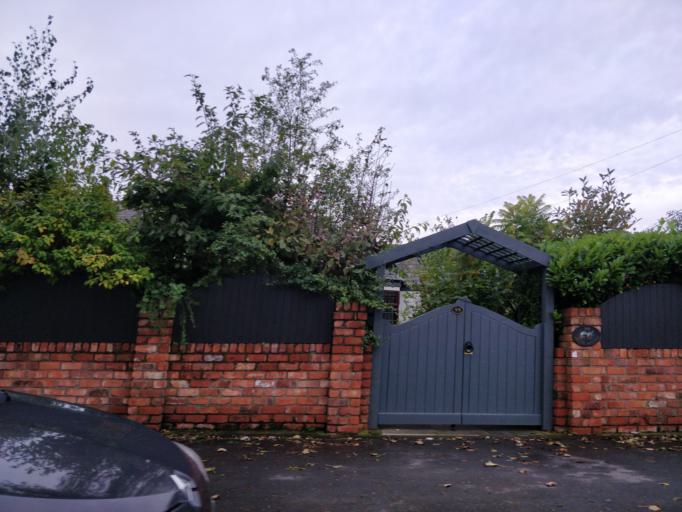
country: GB
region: England
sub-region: Sefton
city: Southport
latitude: 53.6669
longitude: -2.9699
